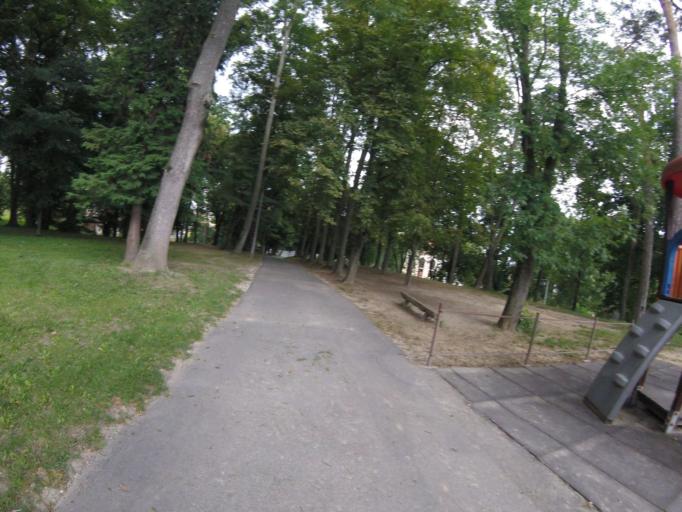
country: HU
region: Zala
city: Nagykanizsa
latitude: 46.4897
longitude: 17.0504
